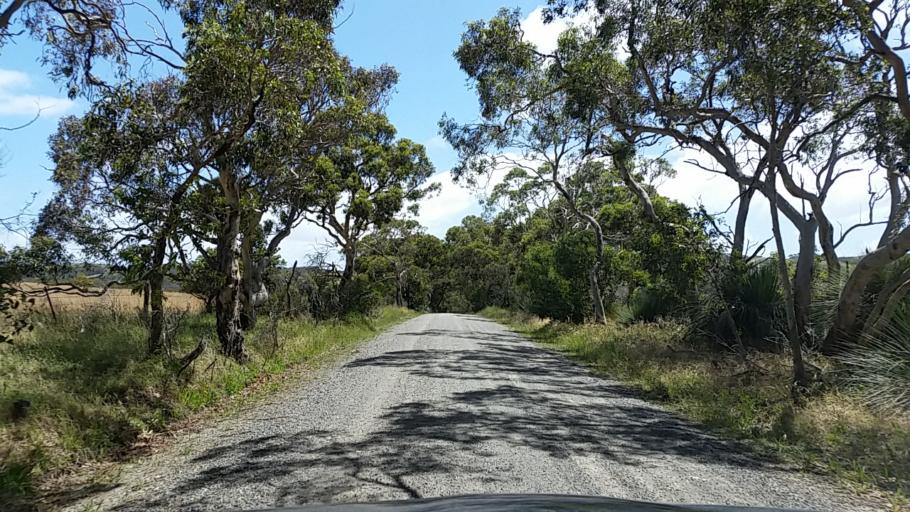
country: AU
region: South Australia
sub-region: Alexandrina
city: Mount Compass
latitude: -35.4365
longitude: 138.5877
